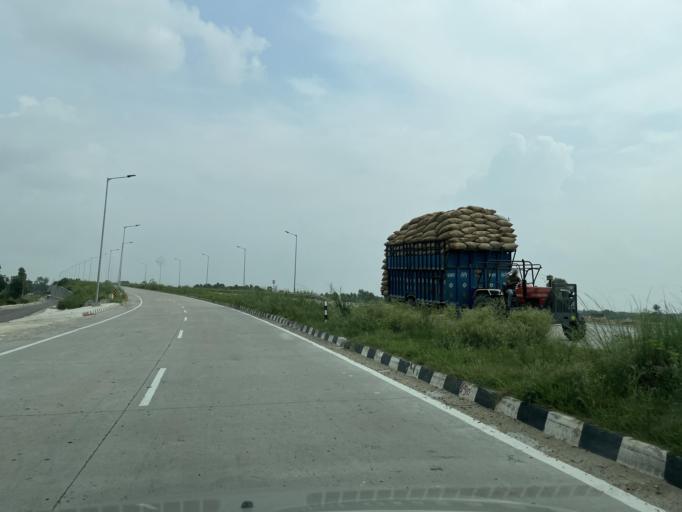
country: IN
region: Uttarakhand
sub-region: Udham Singh Nagar
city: Kashipur
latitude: 29.1767
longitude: 78.9407
